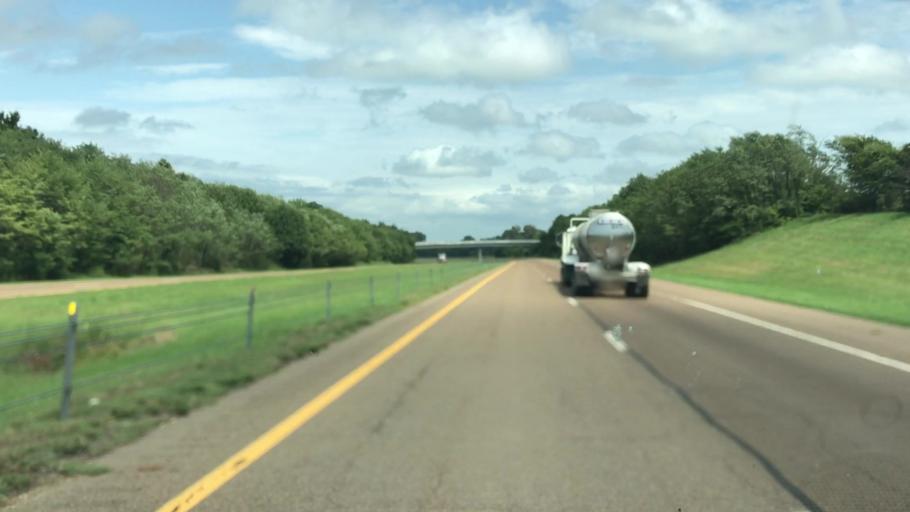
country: US
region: Tennessee
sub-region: Obion County
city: Union City
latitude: 36.4585
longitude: -88.9922
